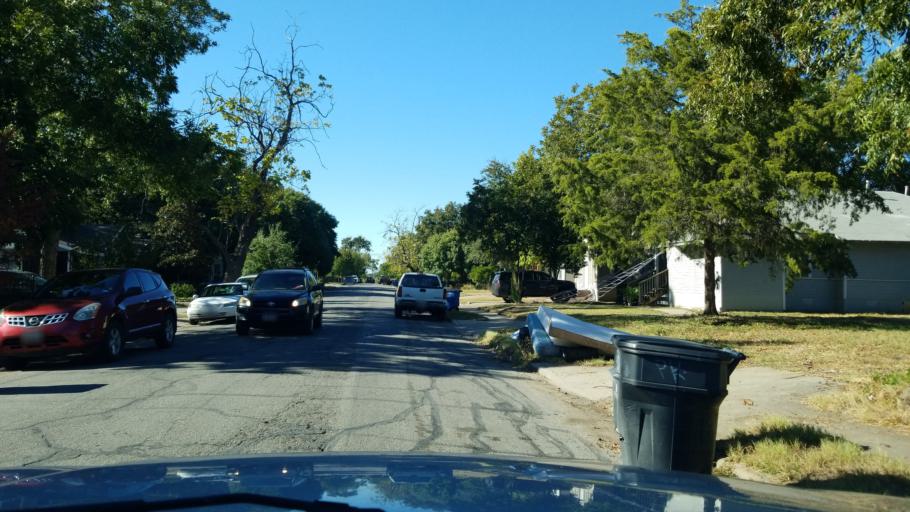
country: US
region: Texas
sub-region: Dallas County
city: Highland Park
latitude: 32.7973
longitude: -96.7451
